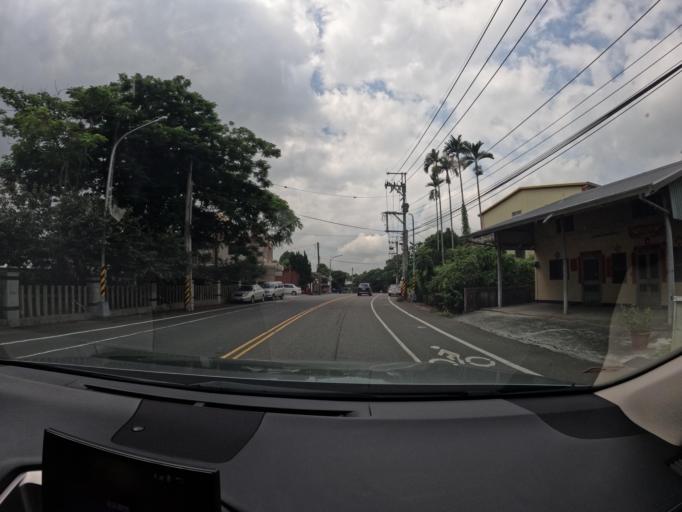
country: TW
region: Taiwan
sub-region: Nantou
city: Nantou
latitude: 23.9250
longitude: 120.6381
